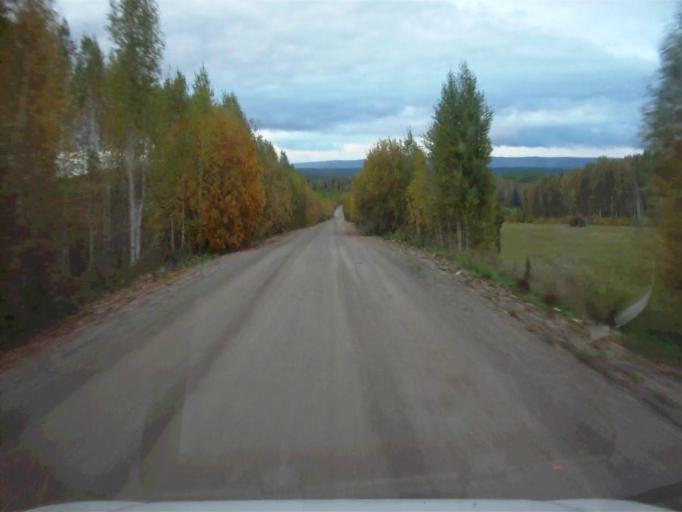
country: RU
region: Sverdlovsk
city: Mikhaylovsk
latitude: 56.2034
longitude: 59.2018
